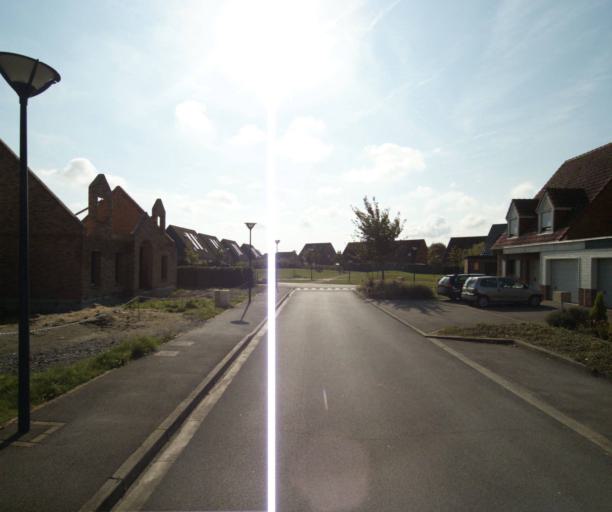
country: FR
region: Nord-Pas-de-Calais
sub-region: Departement du Nord
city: Lompret
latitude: 50.6682
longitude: 2.9805
